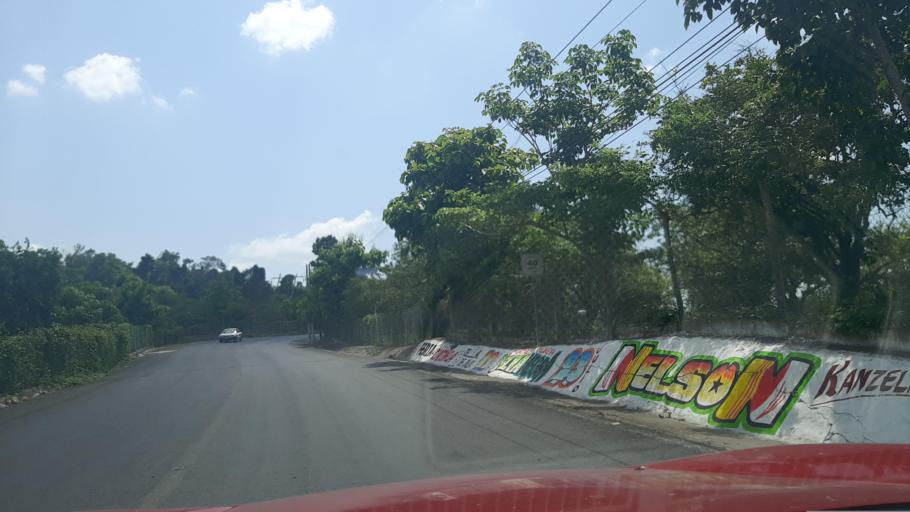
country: MX
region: Veracruz
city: Coatzintla
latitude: 20.4986
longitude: -97.4397
